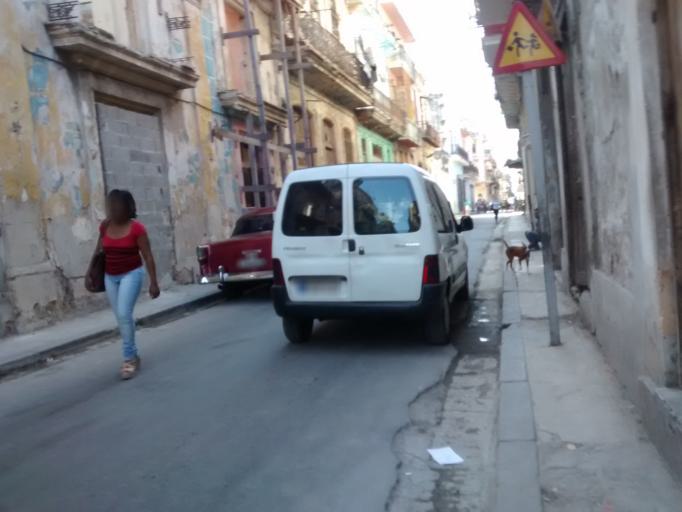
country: CU
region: La Habana
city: La Habana Vieja
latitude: 23.1335
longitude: -82.3505
